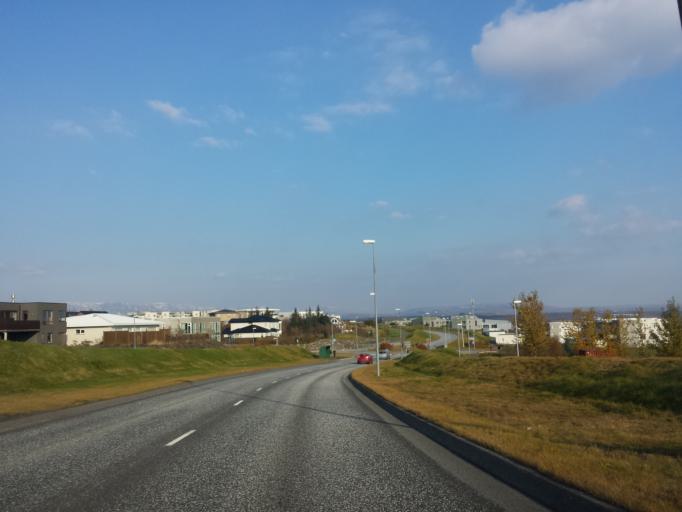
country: IS
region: Capital Region
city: Reykjavik
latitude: 64.0865
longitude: -21.8144
